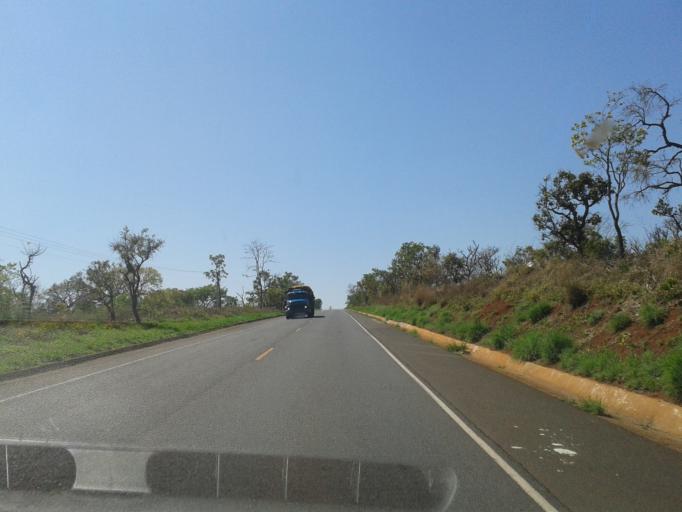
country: BR
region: Minas Gerais
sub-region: Uberlandia
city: Uberlandia
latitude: -19.1126
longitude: -47.9712
